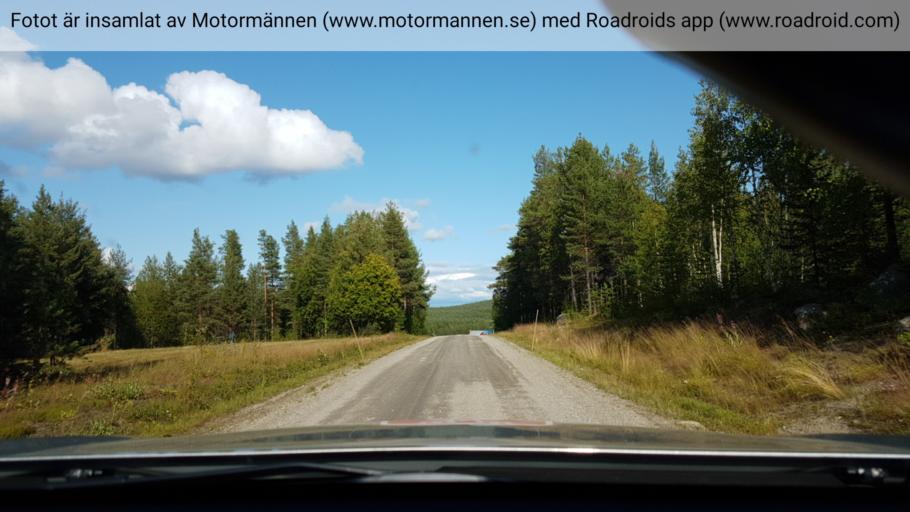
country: SE
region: Vaesterbotten
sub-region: Norsjo Kommun
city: Norsjoe
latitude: 64.6930
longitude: 19.1465
